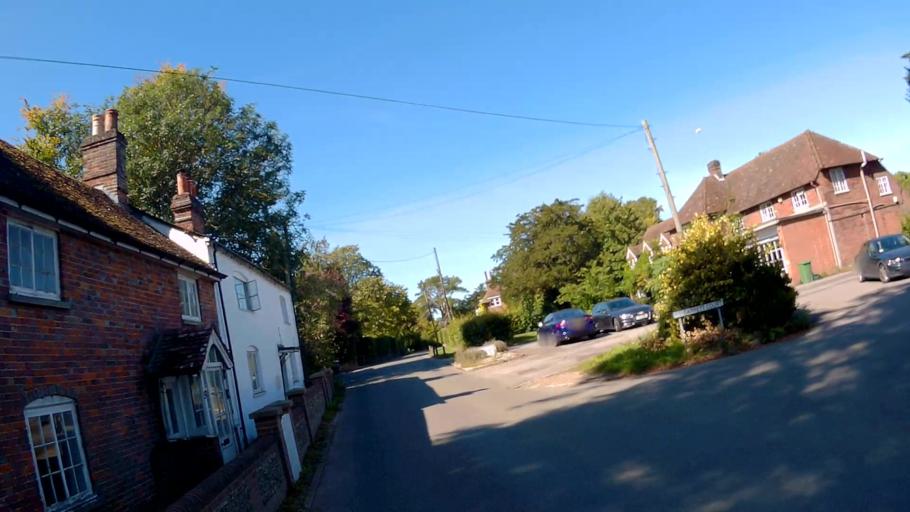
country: GB
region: England
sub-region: Hampshire
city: Overton
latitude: 51.2473
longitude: -1.1809
